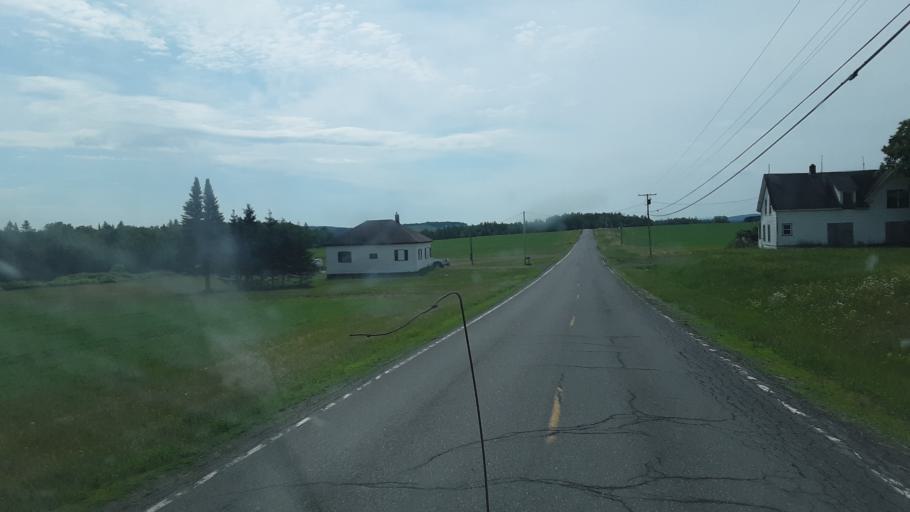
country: US
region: Maine
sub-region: Aroostook County
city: Caribou
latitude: 46.8274
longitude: -68.1752
